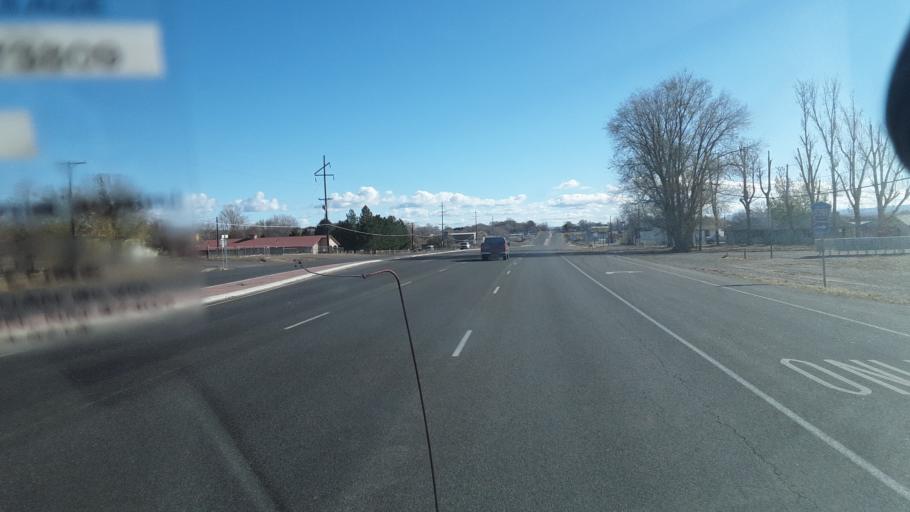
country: US
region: New Mexico
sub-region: San Juan County
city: Lee Acres
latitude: 36.7010
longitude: -108.0717
